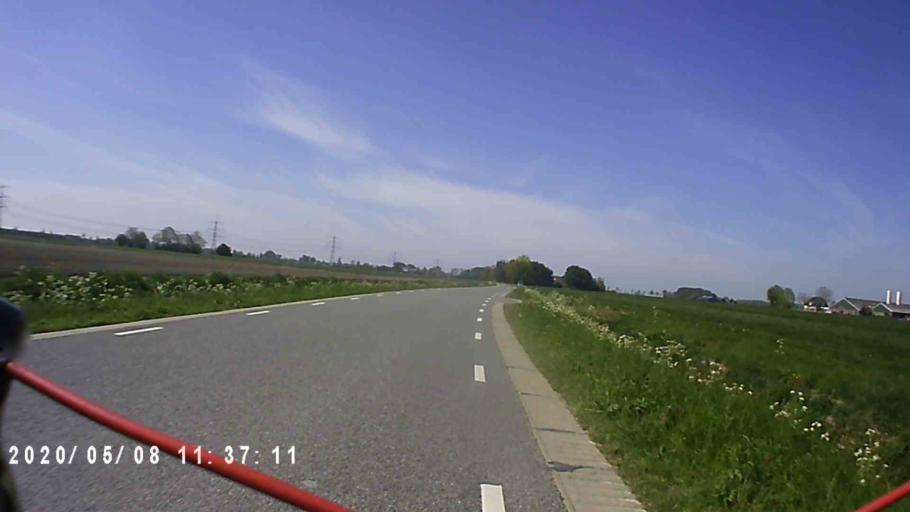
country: NL
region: Groningen
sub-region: Gemeente Bedum
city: Bedum
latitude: 53.3368
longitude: 6.7028
